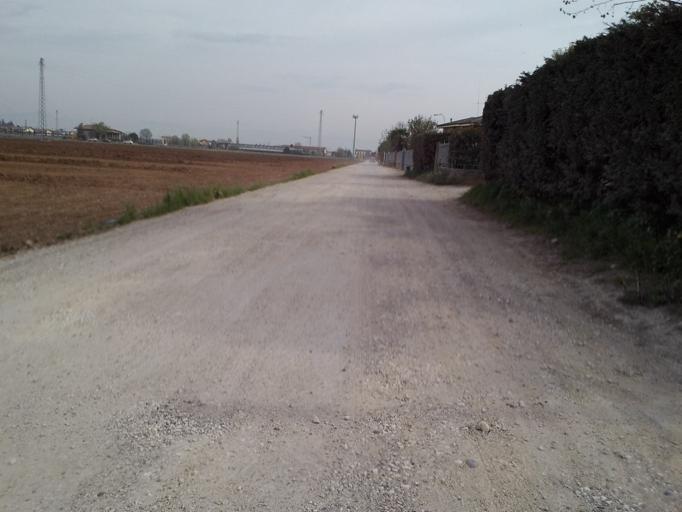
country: IT
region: Veneto
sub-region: Provincia di Verona
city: Villafranca di Verona
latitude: 45.3449
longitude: 10.8532
